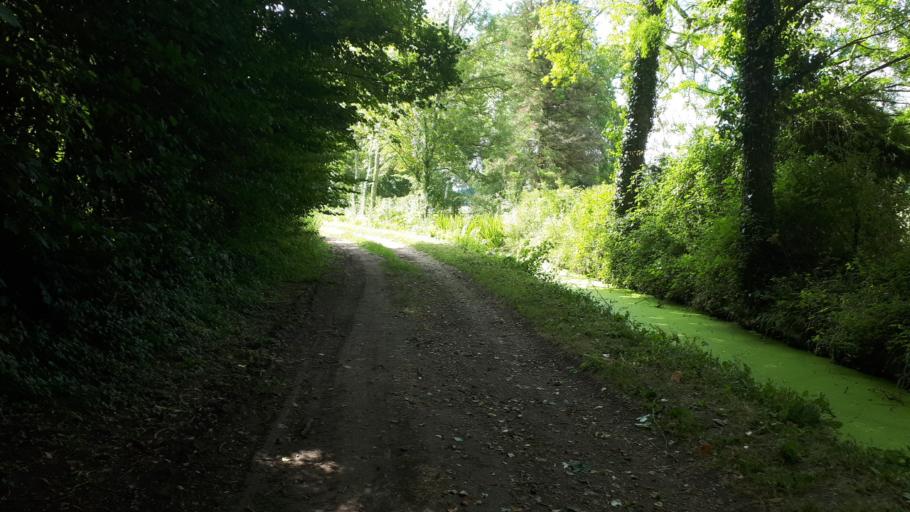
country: FR
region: Centre
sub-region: Departement du Loir-et-Cher
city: Villiers-sur-Loir
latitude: 47.7967
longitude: 0.9841
